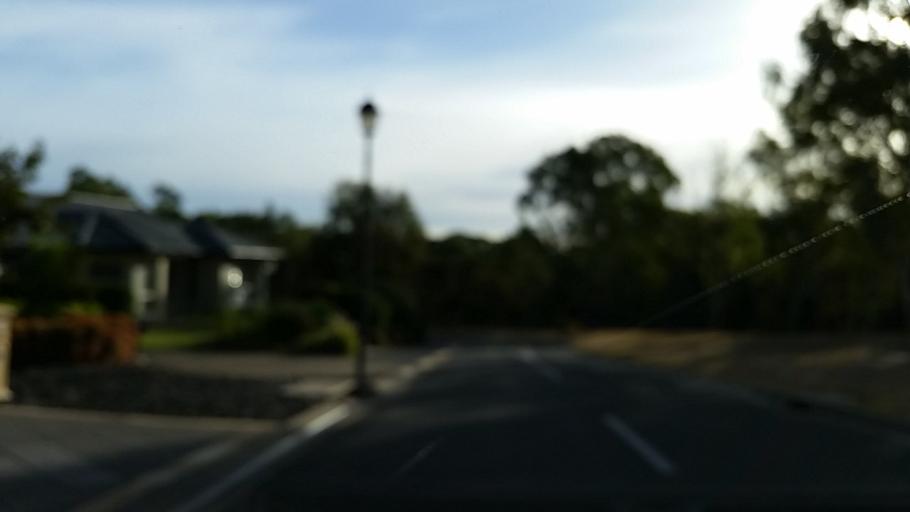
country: AU
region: South Australia
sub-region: Campbelltown
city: Athelstone
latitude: -34.8595
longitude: 138.7101
